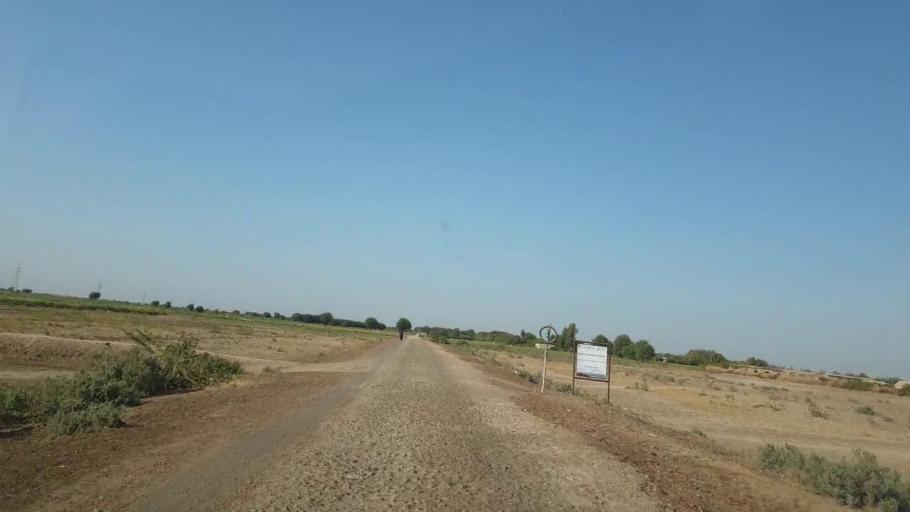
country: PK
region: Sindh
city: Kunri
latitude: 25.0442
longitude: 69.4420
